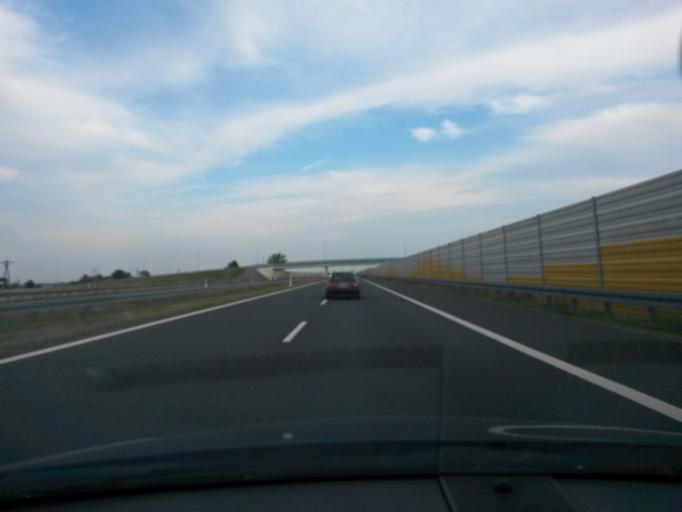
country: PL
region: Lodz Voivodeship
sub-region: Powiat leczycki
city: Swinice Warckie
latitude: 52.0199
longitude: 18.9342
